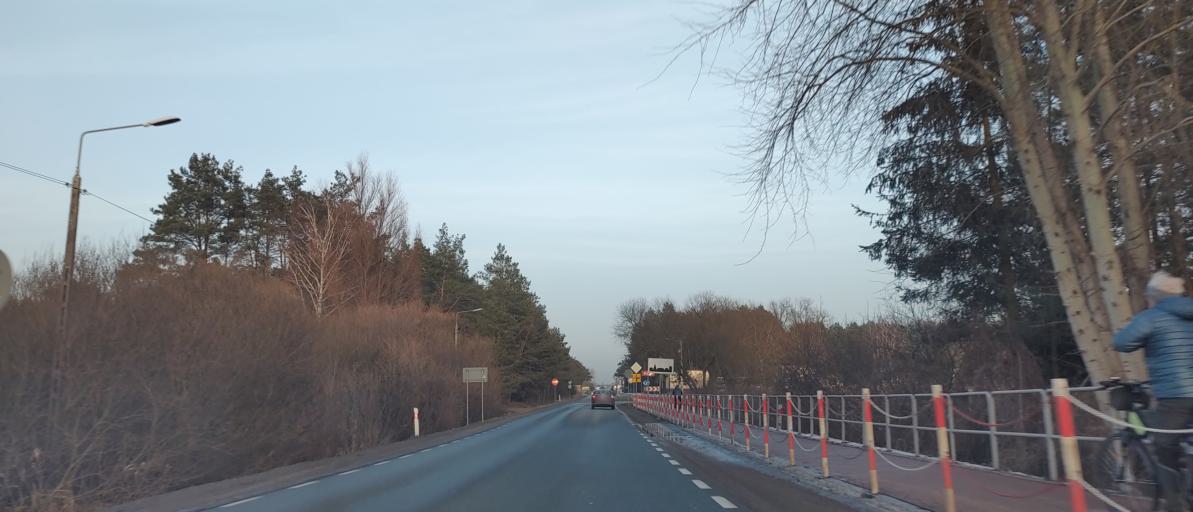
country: PL
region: Masovian Voivodeship
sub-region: Powiat bialobrzeski
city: Bialobrzegi
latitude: 51.6453
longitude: 20.9310
